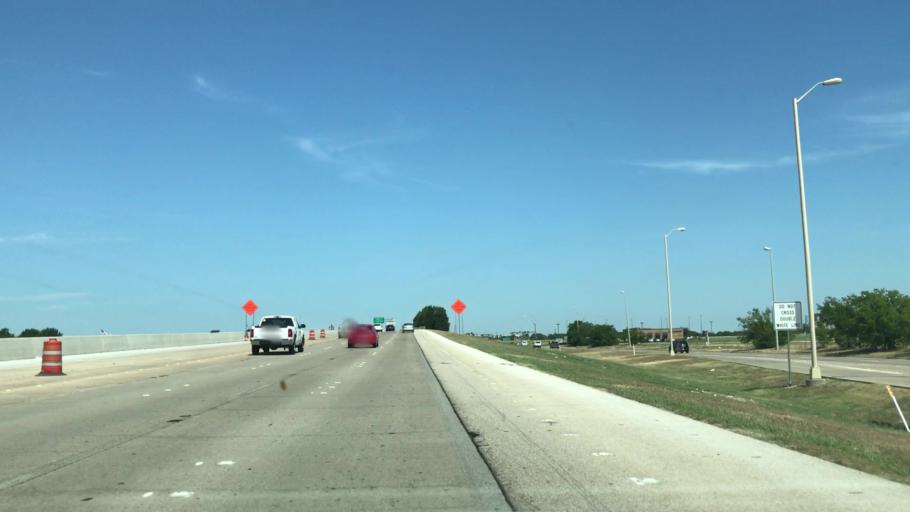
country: US
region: Texas
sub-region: Dallas County
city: Sachse
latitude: 32.9640
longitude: -96.6391
